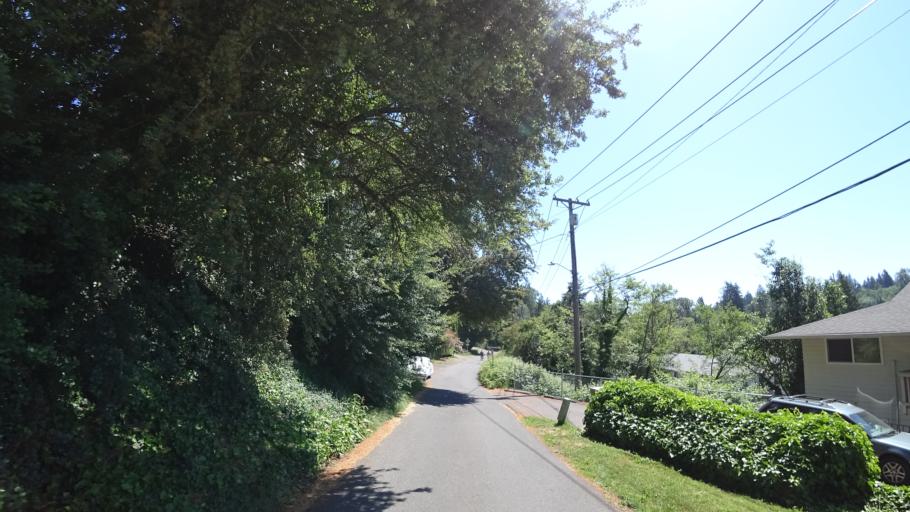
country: US
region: Oregon
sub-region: Washington County
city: Raleigh Hills
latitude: 45.4877
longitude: -122.7246
